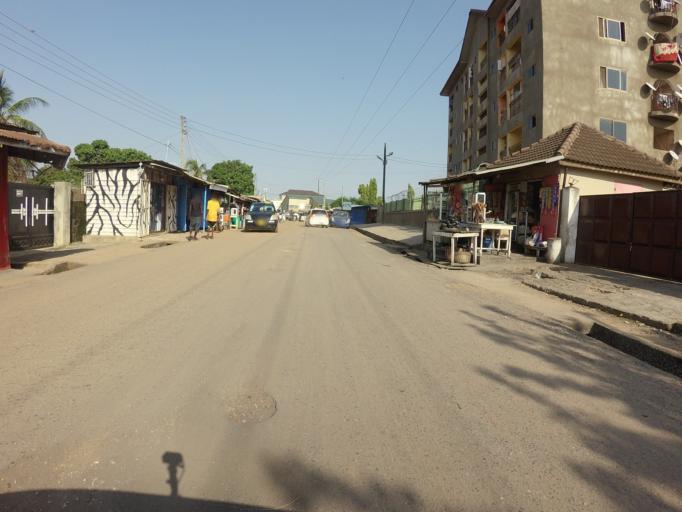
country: GH
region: Greater Accra
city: Dome
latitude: 5.6132
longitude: -0.2381
